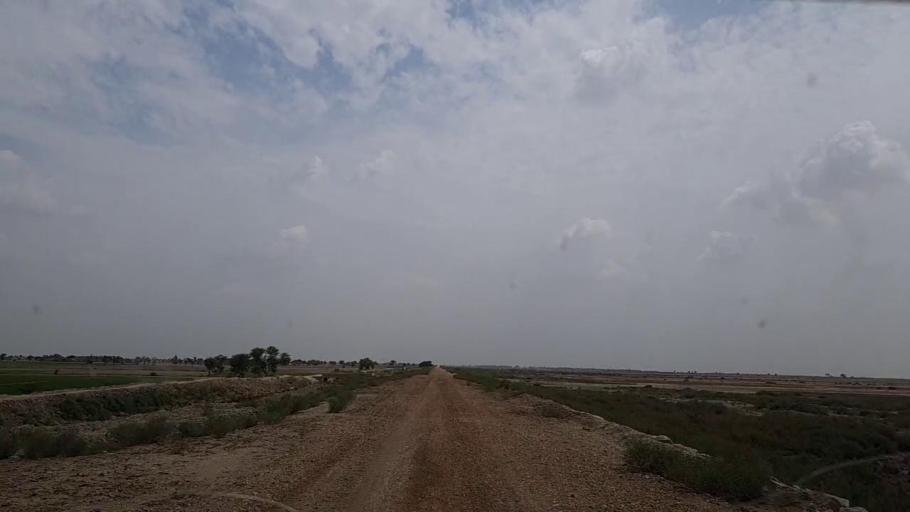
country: PK
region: Sindh
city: Johi
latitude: 26.7871
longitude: 67.5995
